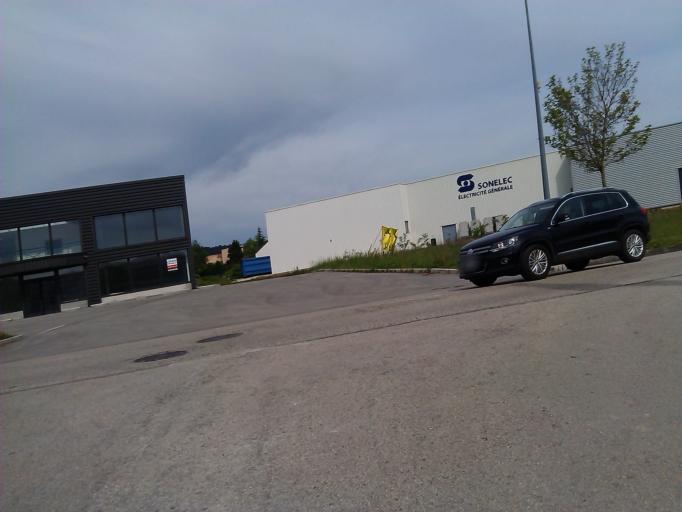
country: FR
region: Franche-Comte
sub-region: Departement du Jura
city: Dole
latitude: 47.1075
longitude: 5.5059
